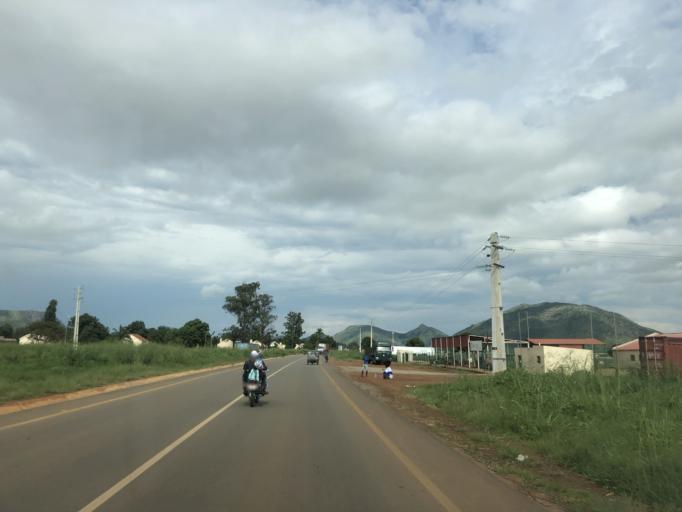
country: AO
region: Cuanza Sul
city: Uacu Cungo
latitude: -11.3514
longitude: 15.1113
